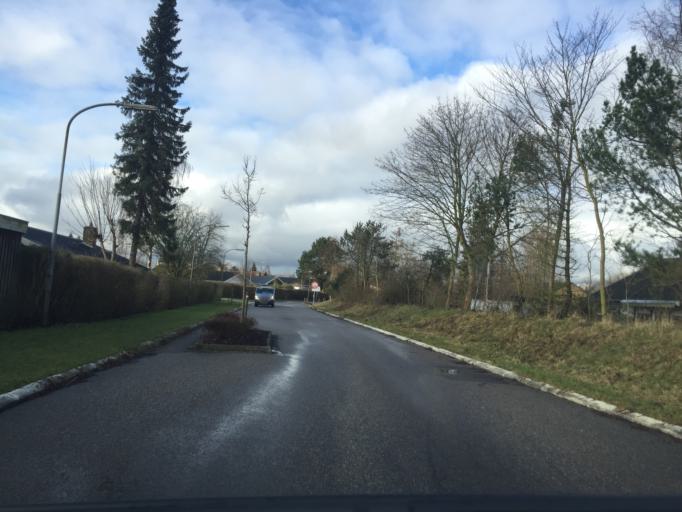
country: DK
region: Capital Region
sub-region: Fureso Kommune
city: Stavnsholt
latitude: 55.8116
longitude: 12.3991
